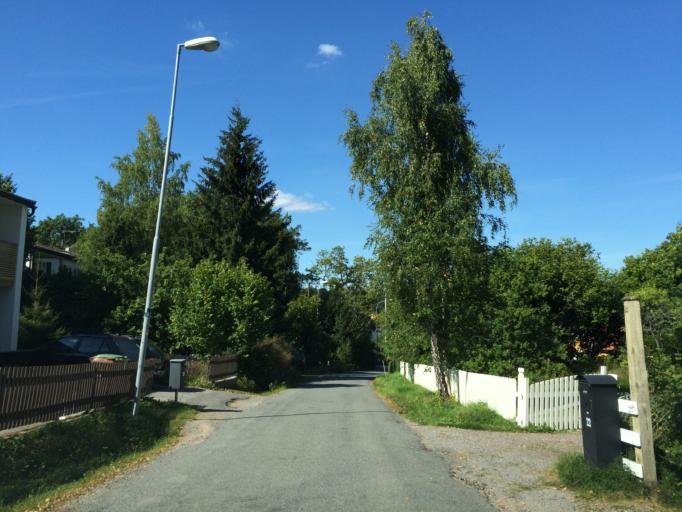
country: SE
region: Stockholm
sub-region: Sollentuna Kommun
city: Sollentuna
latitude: 59.4547
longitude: 17.9106
